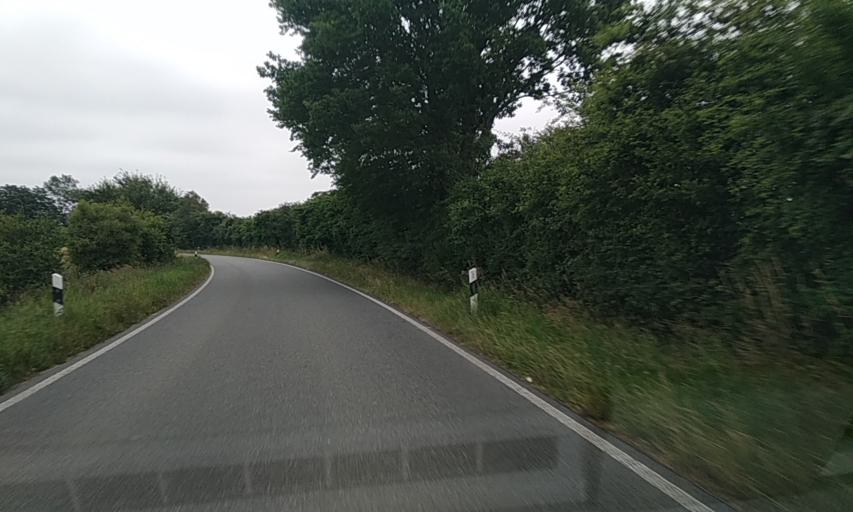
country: DE
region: Schleswig-Holstein
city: Loit
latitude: 54.6055
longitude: 9.7219
